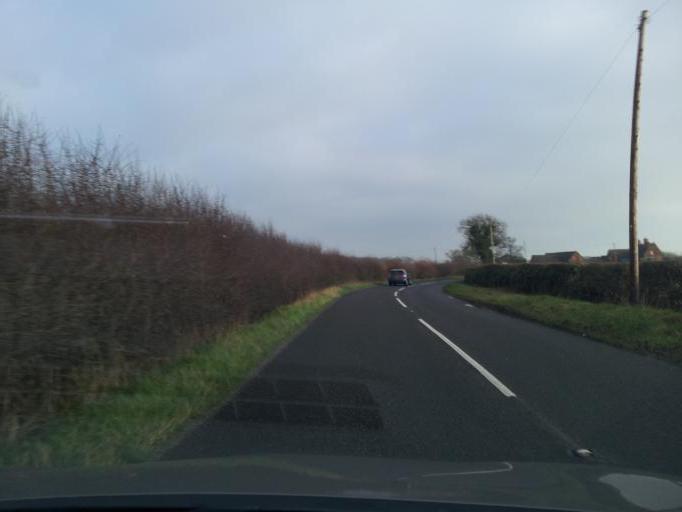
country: GB
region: England
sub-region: Derbyshire
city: Rodsley
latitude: 52.8787
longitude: -1.7452
